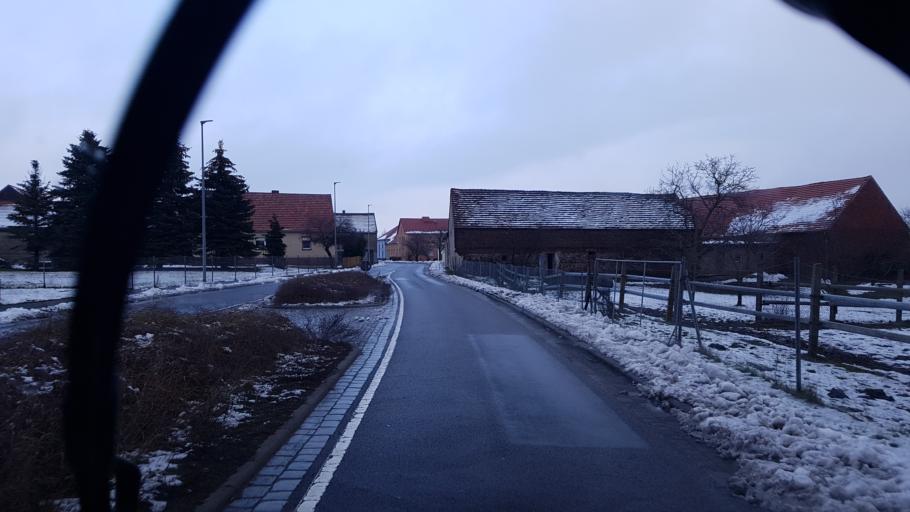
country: DE
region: Brandenburg
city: Heinersbruck
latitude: 51.8468
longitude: 14.5869
